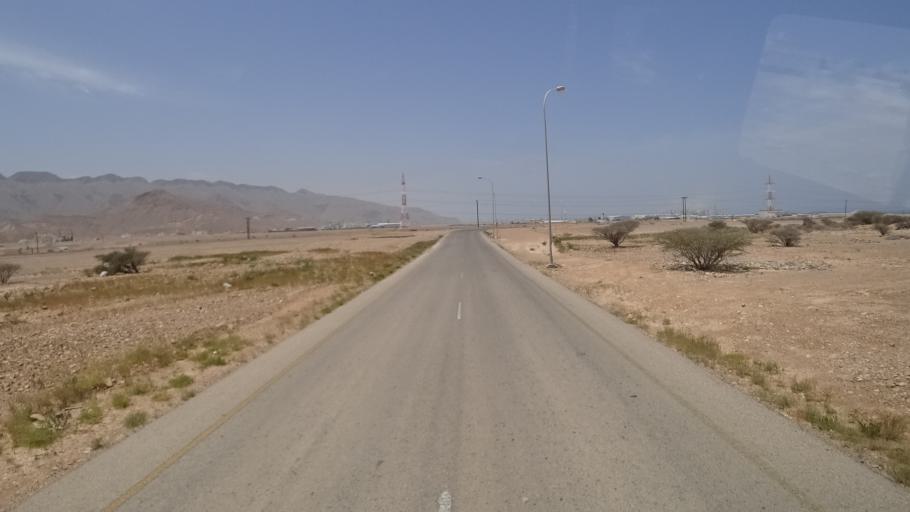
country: OM
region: Ash Sharqiyah
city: Sur
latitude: 22.6060
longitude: 59.4350
